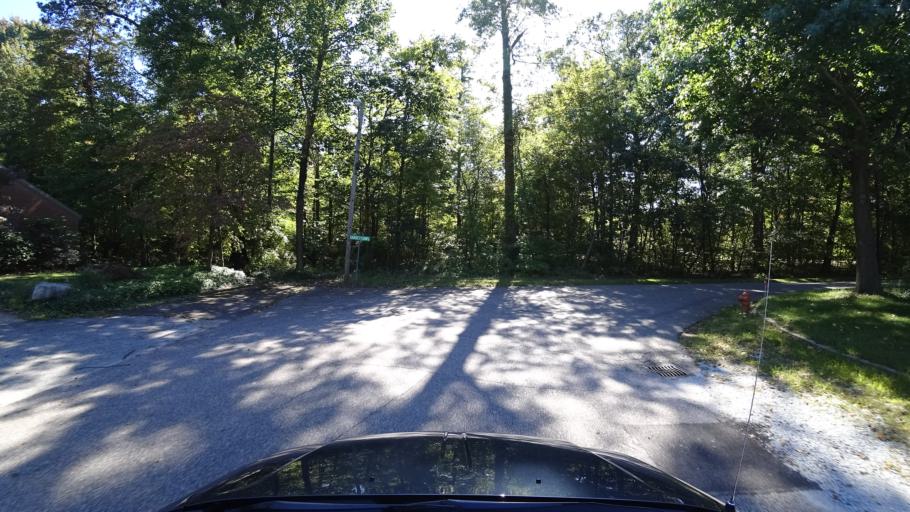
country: US
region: Indiana
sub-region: LaPorte County
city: Michigan City
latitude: 41.6913
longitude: -86.8830
